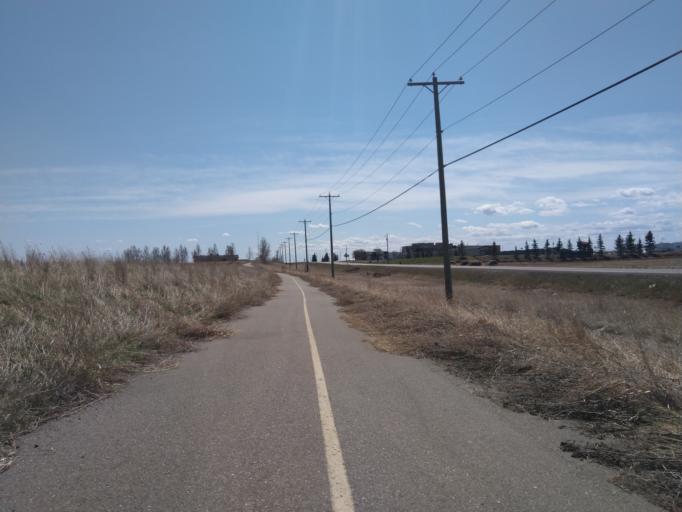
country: CA
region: Alberta
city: Chestermere
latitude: 50.9591
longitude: -113.9115
